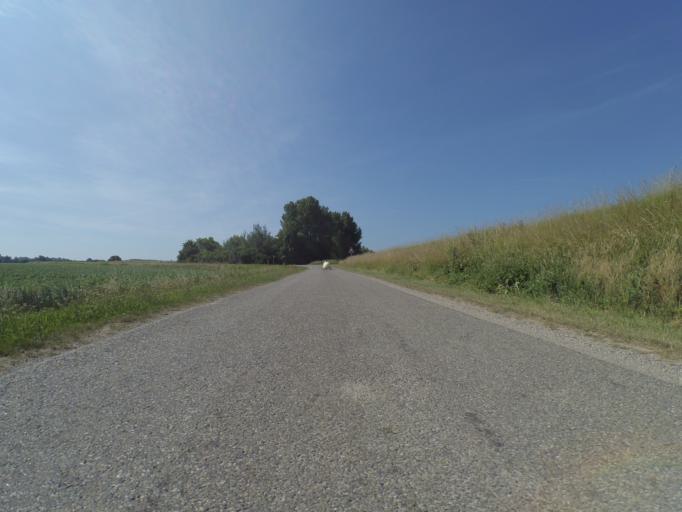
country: NL
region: North Brabant
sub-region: Gemeente Steenbergen
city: Nieuw-Vossemeer
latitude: 51.6018
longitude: 4.2111
